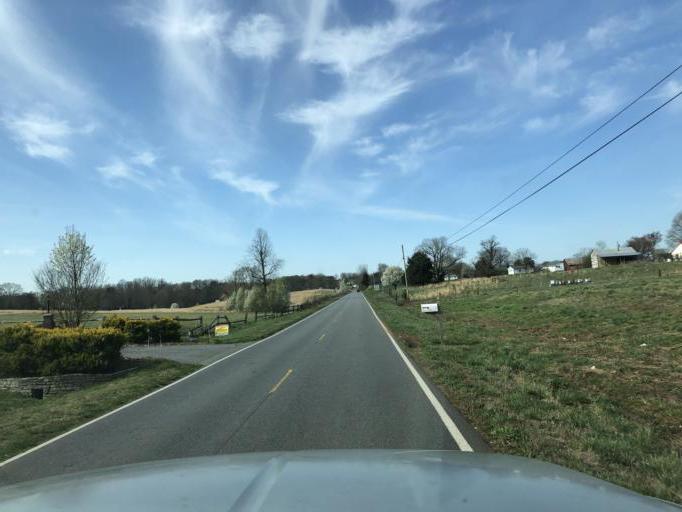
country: US
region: North Carolina
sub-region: Burke County
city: Salem
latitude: 35.5069
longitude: -81.6248
